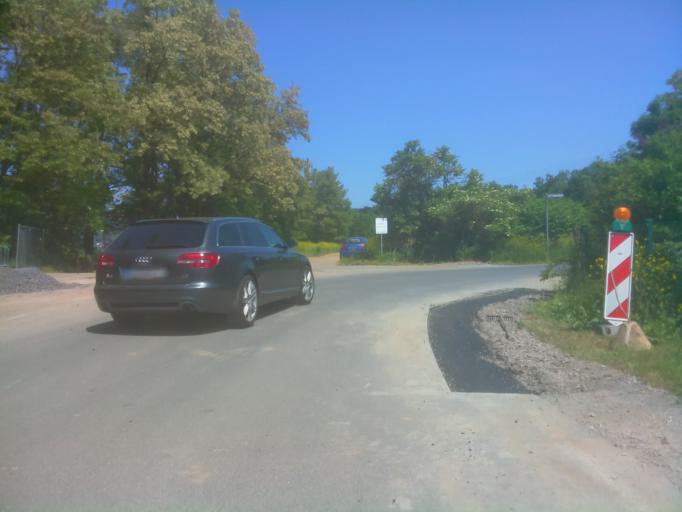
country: DE
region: Thuringia
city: Saalfeld
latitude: 50.6428
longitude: 11.3750
